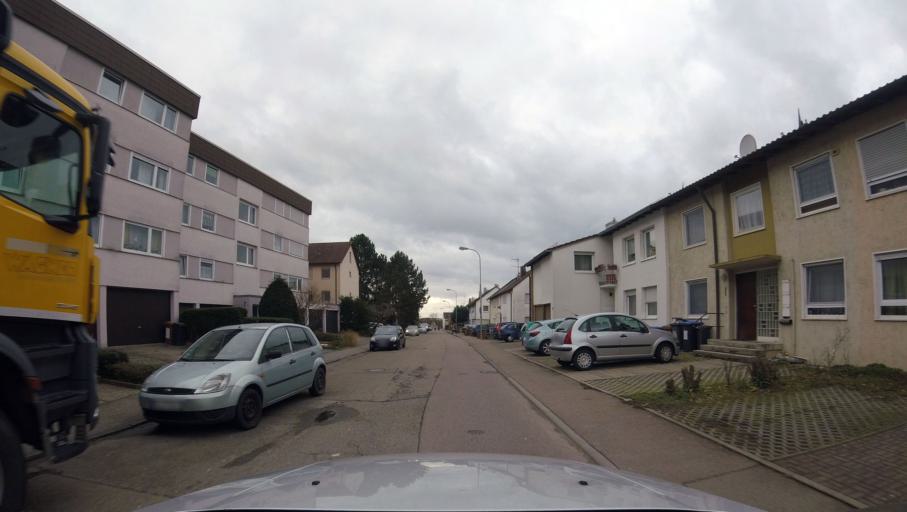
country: DE
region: Baden-Wuerttemberg
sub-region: Regierungsbezirk Stuttgart
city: Backnang
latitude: 48.9576
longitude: 9.4352
